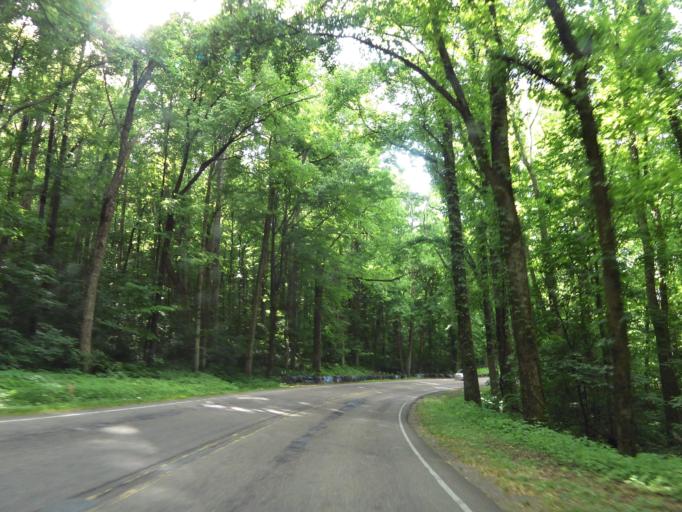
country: US
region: Tennessee
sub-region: Sevier County
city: Gatlinburg
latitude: 35.6400
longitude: -83.5035
